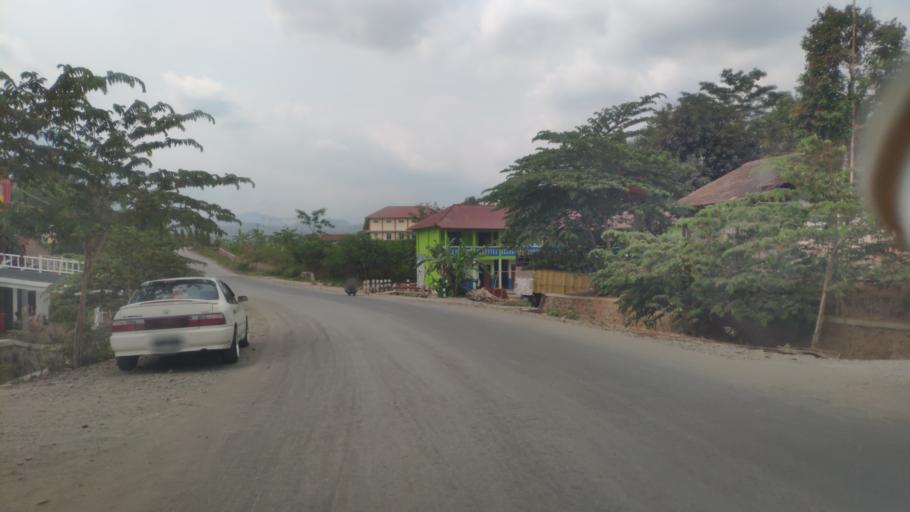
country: ID
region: Central Java
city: Wonosobo
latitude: -7.3843
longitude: 109.6657
